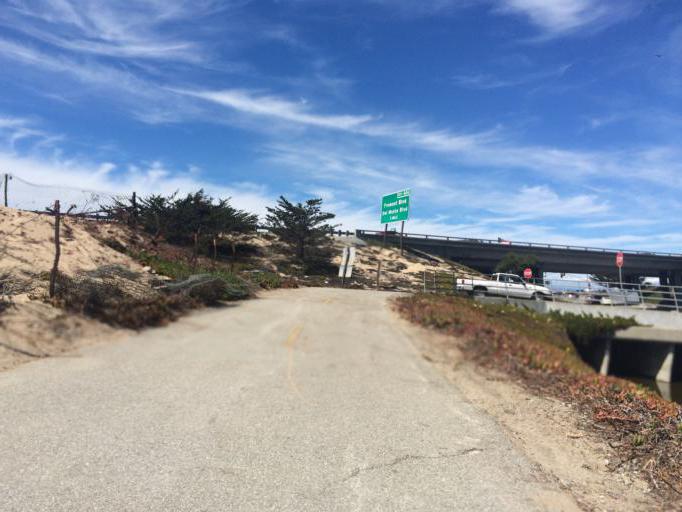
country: US
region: California
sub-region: Monterey County
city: Seaside
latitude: 36.6092
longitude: -121.8581
